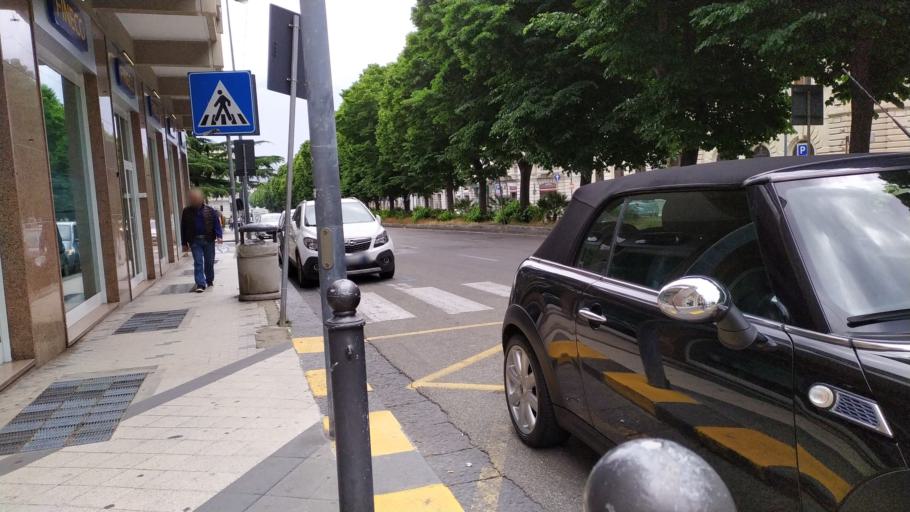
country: IT
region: Sicily
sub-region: Messina
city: Messina
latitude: 38.1882
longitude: 15.5562
